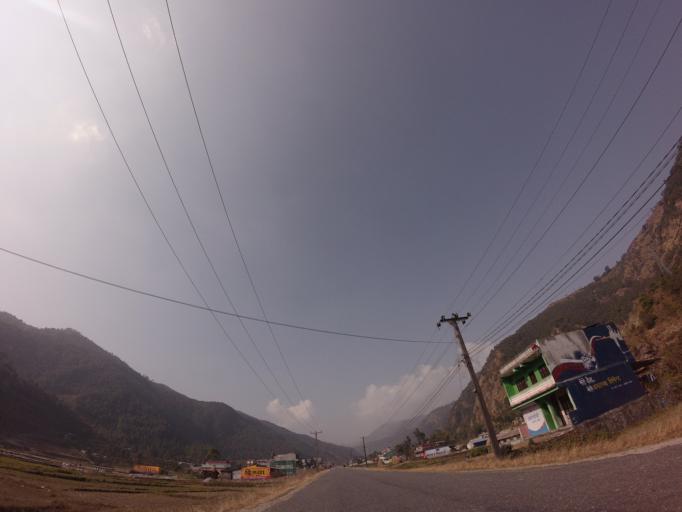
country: NP
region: Western Region
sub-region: Gandaki Zone
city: Pokhara
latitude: 28.2852
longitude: 83.9064
